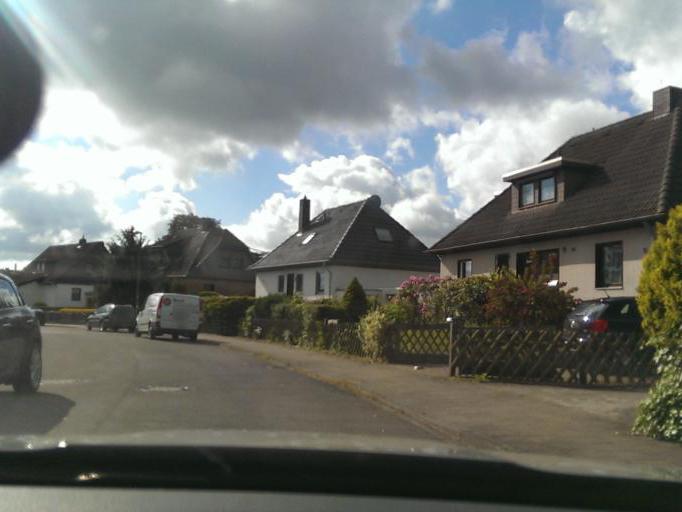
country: DE
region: Lower Saxony
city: Elze
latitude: 52.5542
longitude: 9.7396
